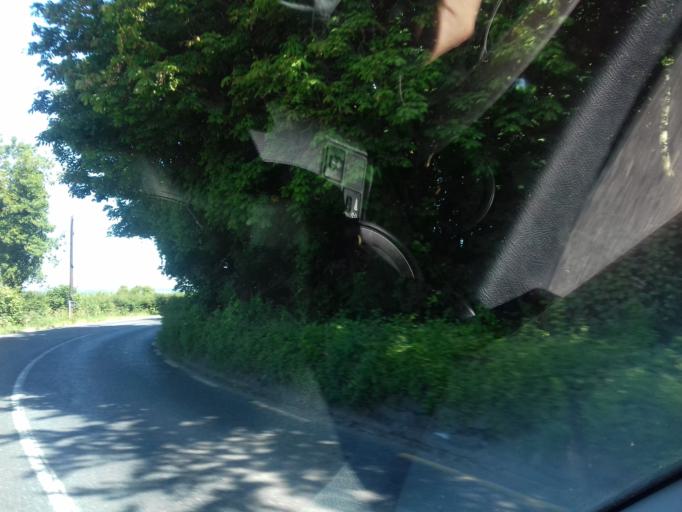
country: IE
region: Leinster
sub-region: Fingal County
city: Swords
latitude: 53.4742
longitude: -6.2730
